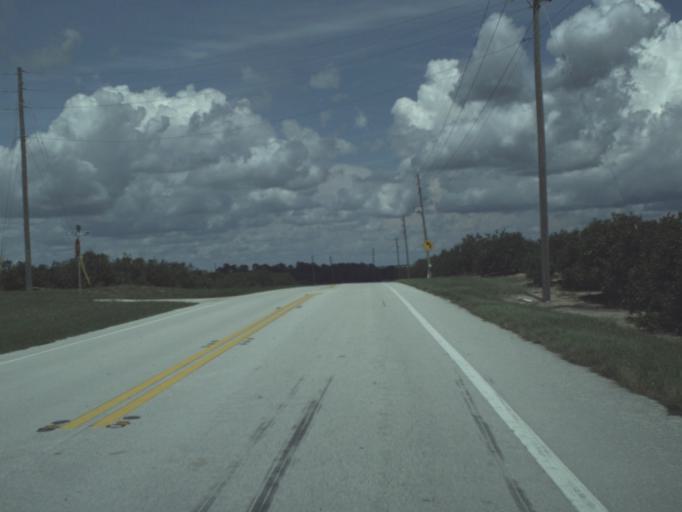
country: US
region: Florida
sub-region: Highlands County
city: Avon Park
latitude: 27.5752
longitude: -81.4654
